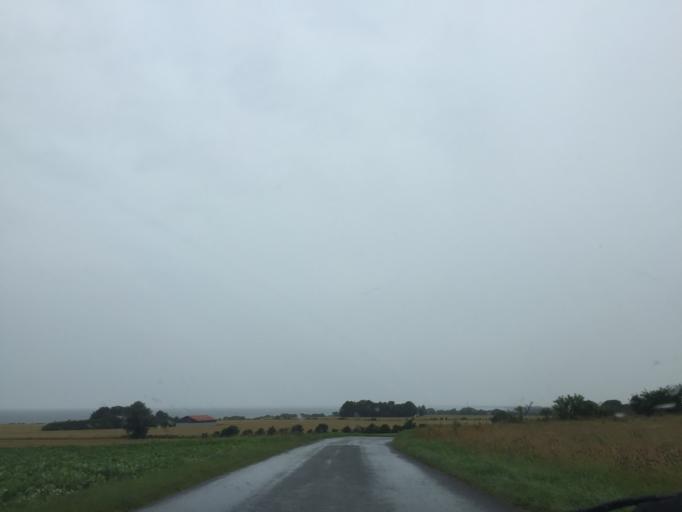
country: DK
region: Zealand
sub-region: Vordingborg Kommune
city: Stege
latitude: 54.9526
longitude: 12.4953
